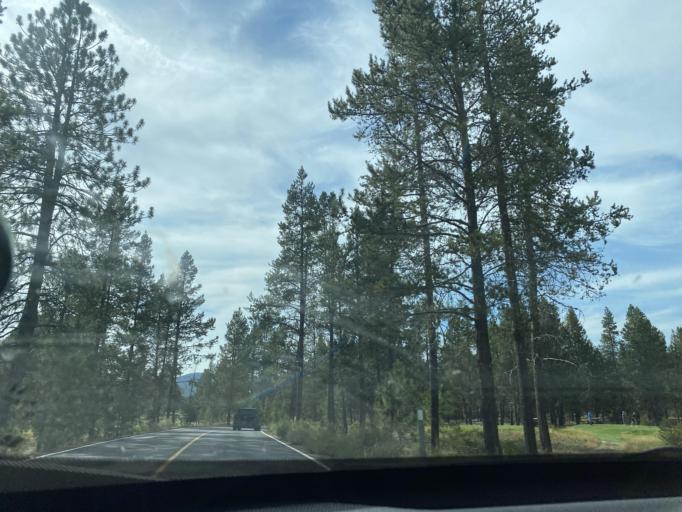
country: US
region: Oregon
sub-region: Deschutes County
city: Sunriver
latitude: 43.8798
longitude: -121.4367
